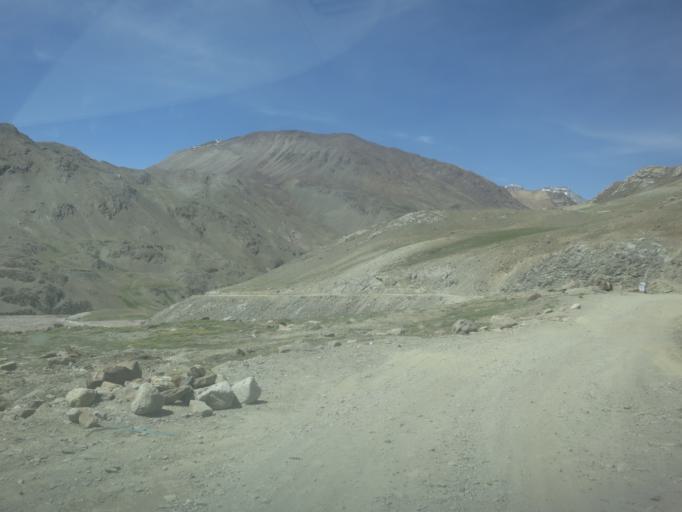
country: IN
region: Himachal Pradesh
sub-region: Kulu
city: Manali
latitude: 32.4059
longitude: 77.6428
